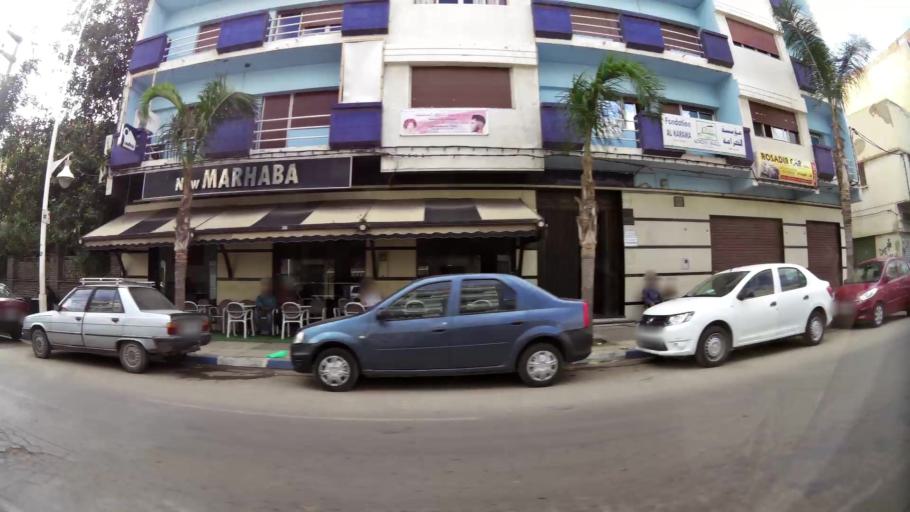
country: MA
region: Oriental
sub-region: Nador
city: Nador
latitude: 35.1739
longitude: -2.9234
